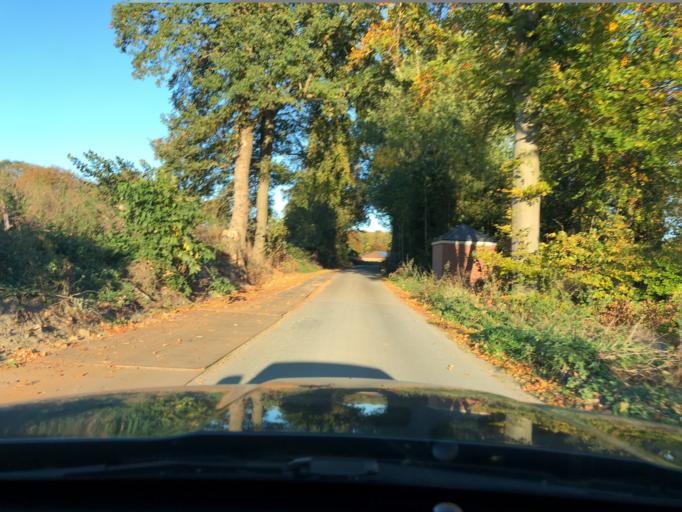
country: DE
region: North Rhine-Westphalia
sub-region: Regierungsbezirk Munster
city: Muenster
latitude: 52.0181
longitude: 7.6963
